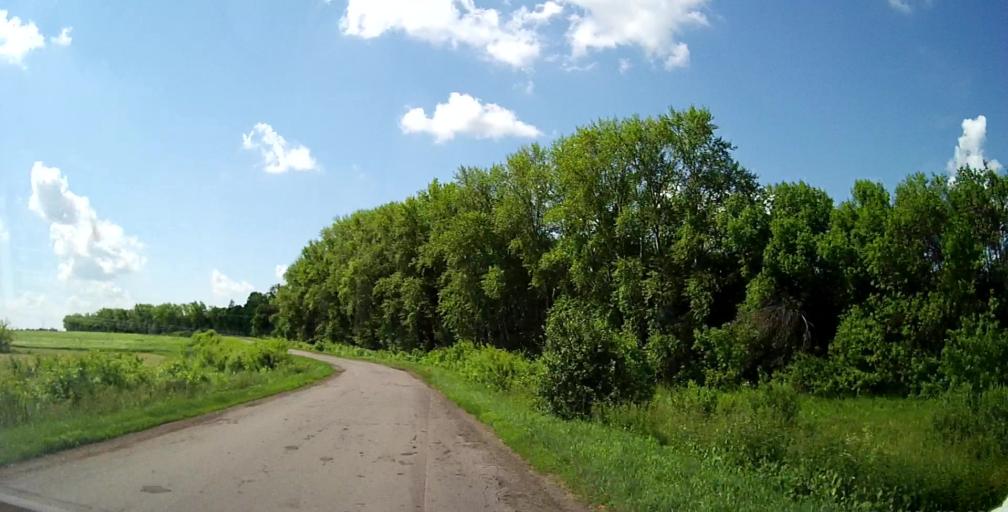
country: RU
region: Lipetsk
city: Chaplygin
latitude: 53.3037
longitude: 39.9520
